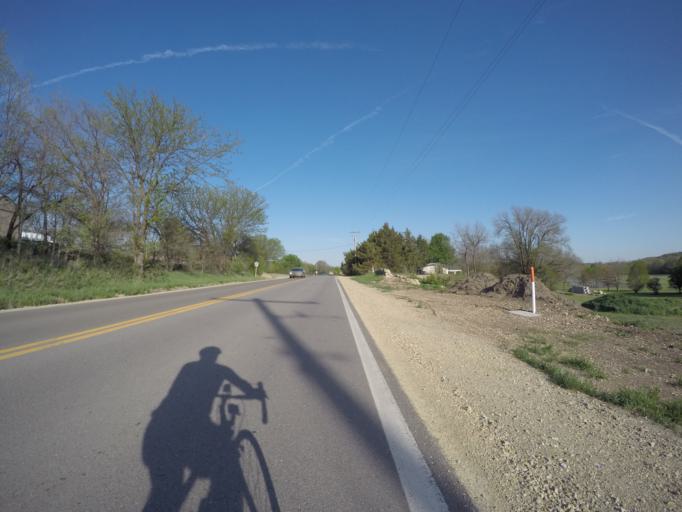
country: US
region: Kansas
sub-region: Riley County
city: Ogden
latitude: 39.2258
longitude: -96.7120
